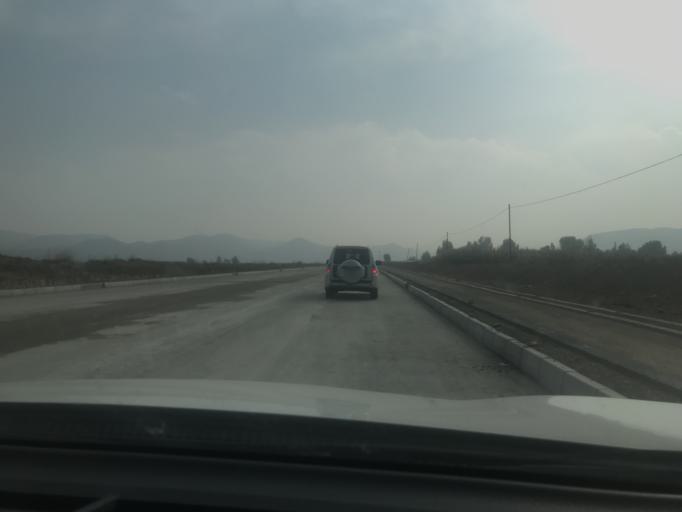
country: CN
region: Gansu Sheng
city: Gulang
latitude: 37.5048
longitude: 102.9013
